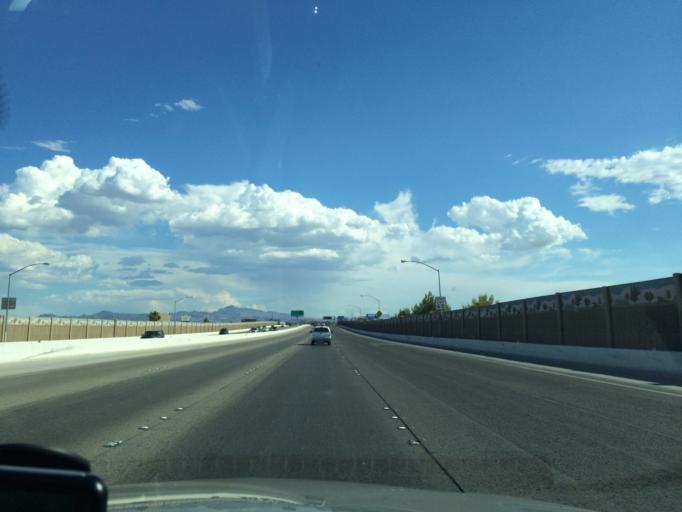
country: US
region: Nevada
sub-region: Clark County
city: Winchester
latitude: 36.1510
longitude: -115.0917
